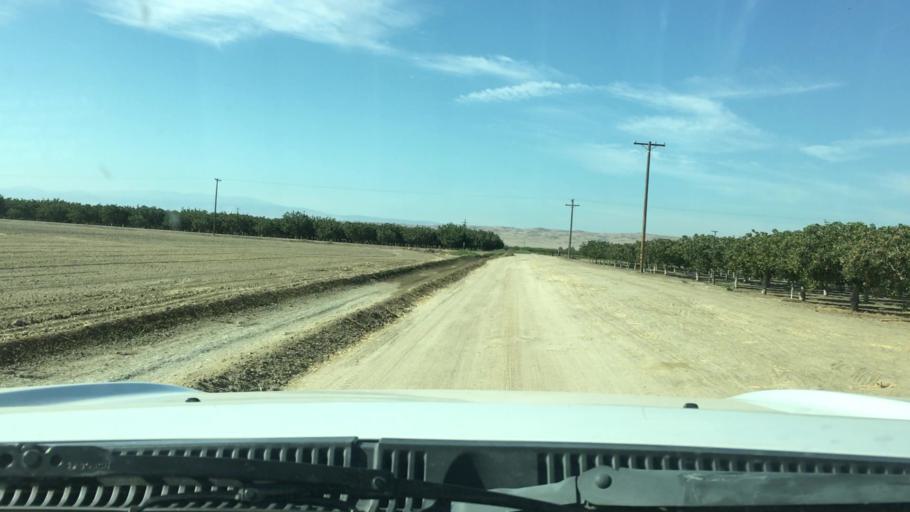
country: US
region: California
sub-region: Kern County
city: Buttonwillow
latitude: 35.3781
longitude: -119.4034
